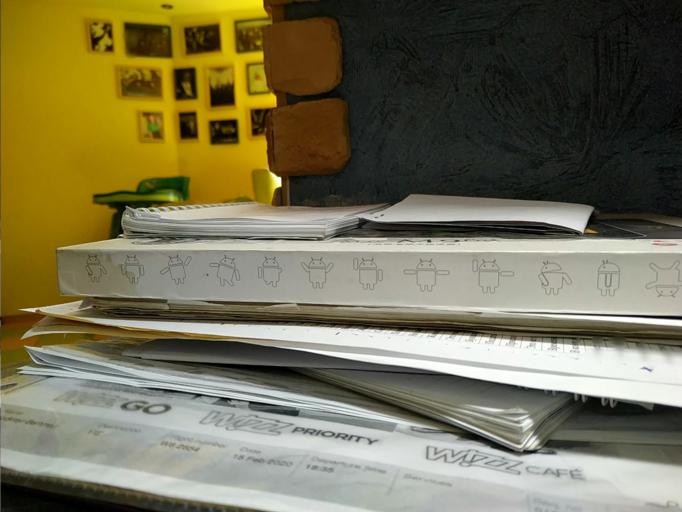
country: RU
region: Novgorod
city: Utorgosh
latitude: 58.2622
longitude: 29.8850
